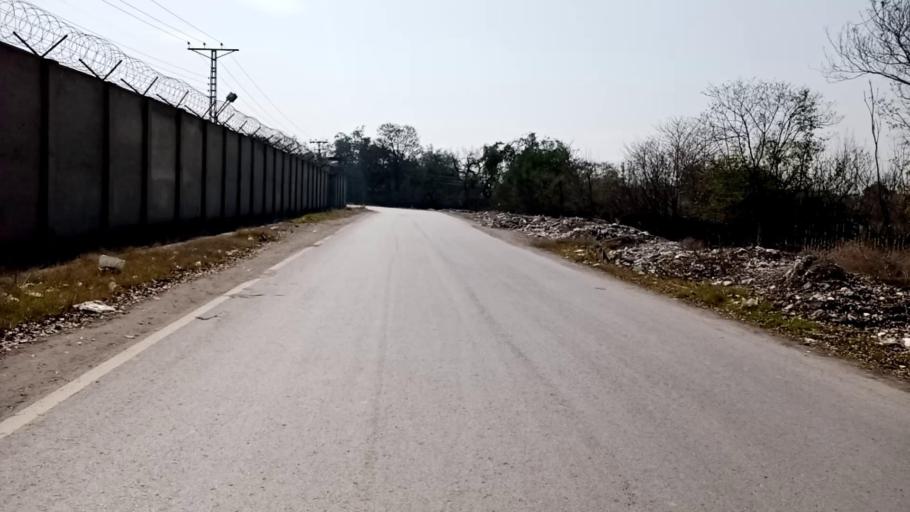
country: PK
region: Khyber Pakhtunkhwa
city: Peshawar
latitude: 33.9926
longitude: 71.5106
